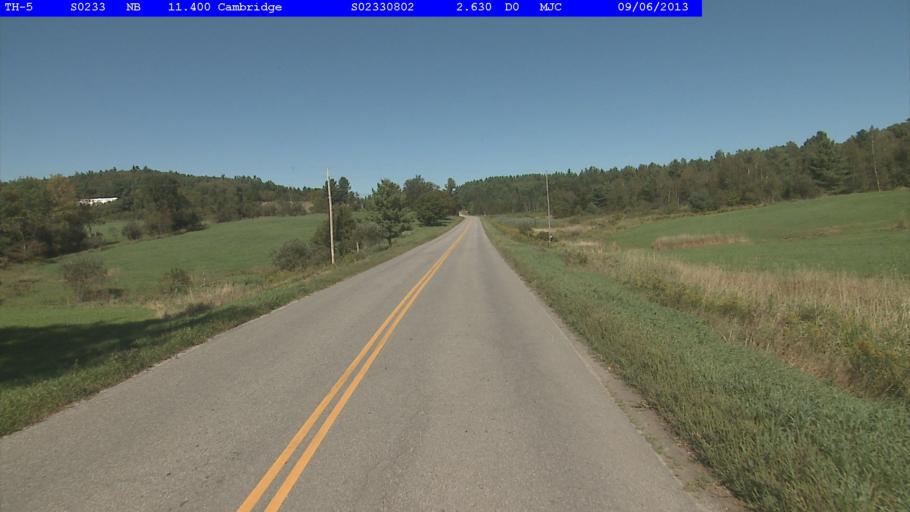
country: US
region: Vermont
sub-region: Lamoille County
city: Johnson
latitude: 44.6194
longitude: -72.8565
